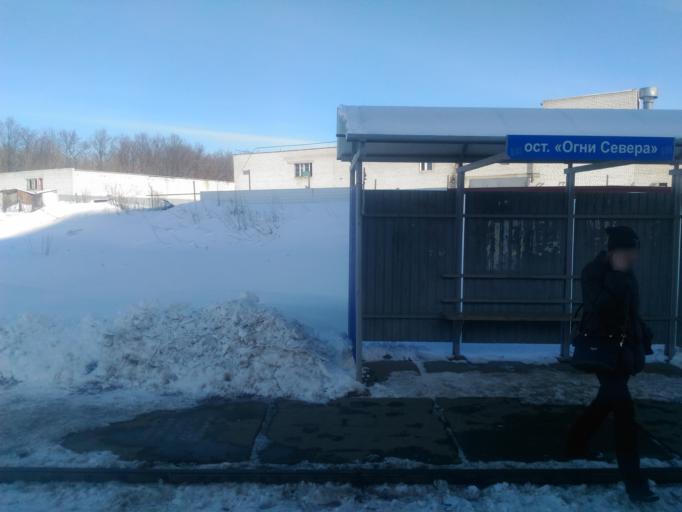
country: RU
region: Ulyanovsk
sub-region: Ulyanovskiy Rayon
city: Ulyanovsk
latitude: 54.3499
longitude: 48.3417
